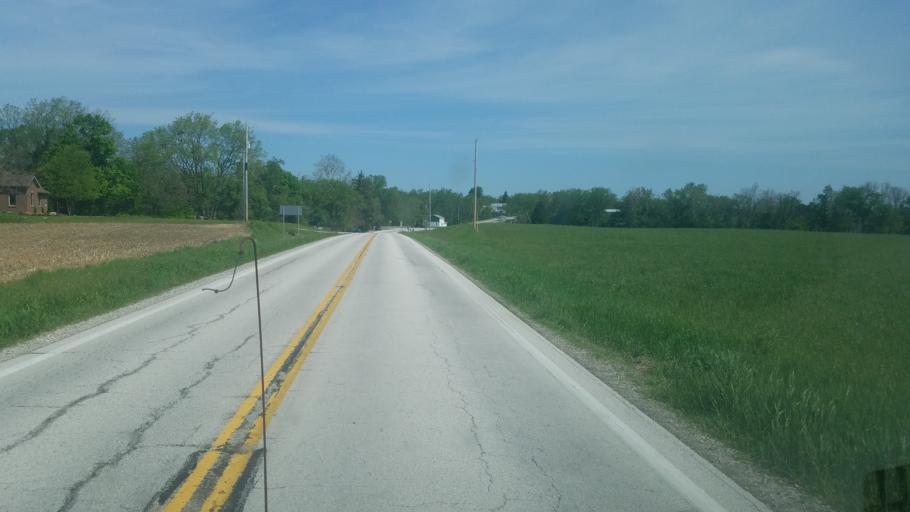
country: US
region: Ohio
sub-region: Seneca County
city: Tiffin
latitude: 41.0177
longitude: -83.1095
